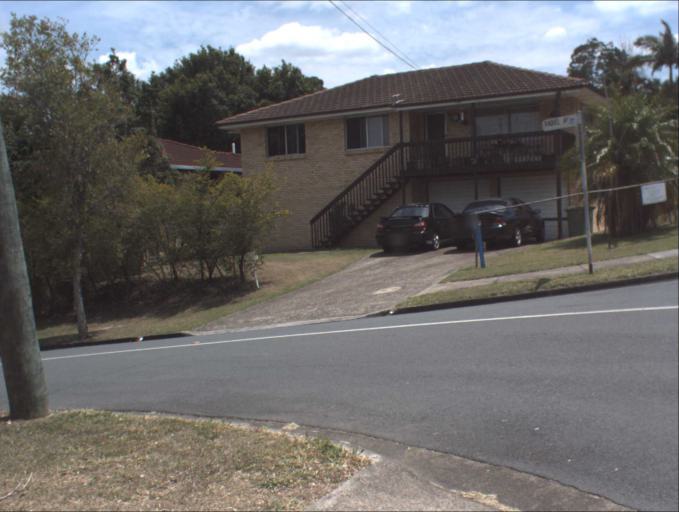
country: AU
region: Queensland
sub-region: Logan
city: Springwood
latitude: -27.6183
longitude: 153.1356
